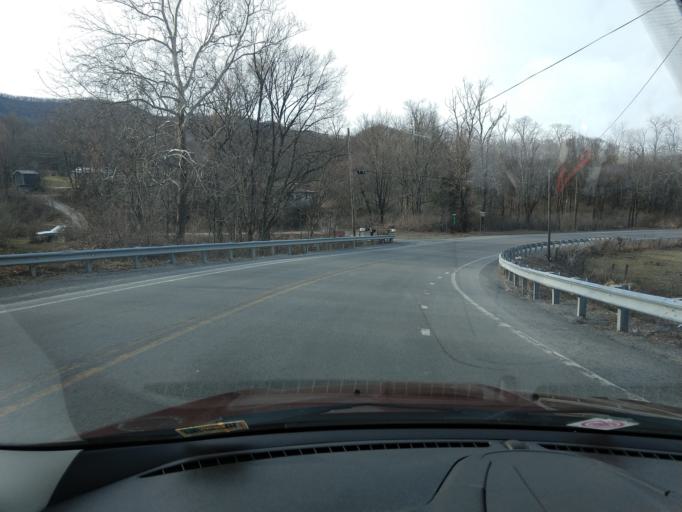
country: US
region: West Virginia
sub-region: Pendleton County
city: Franklin
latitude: 38.7063
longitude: -79.4296
